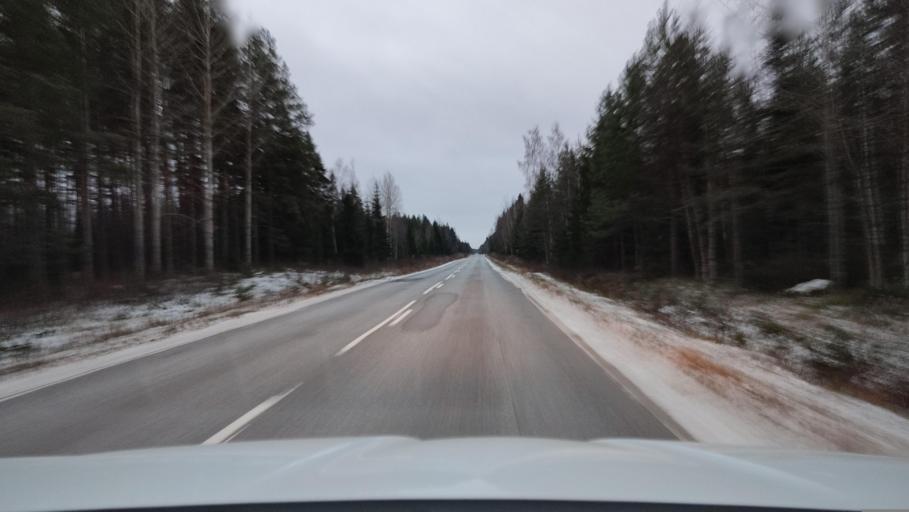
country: FI
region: Ostrobothnia
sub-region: Vaasa
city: Replot
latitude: 63.2626
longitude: 21.3601
